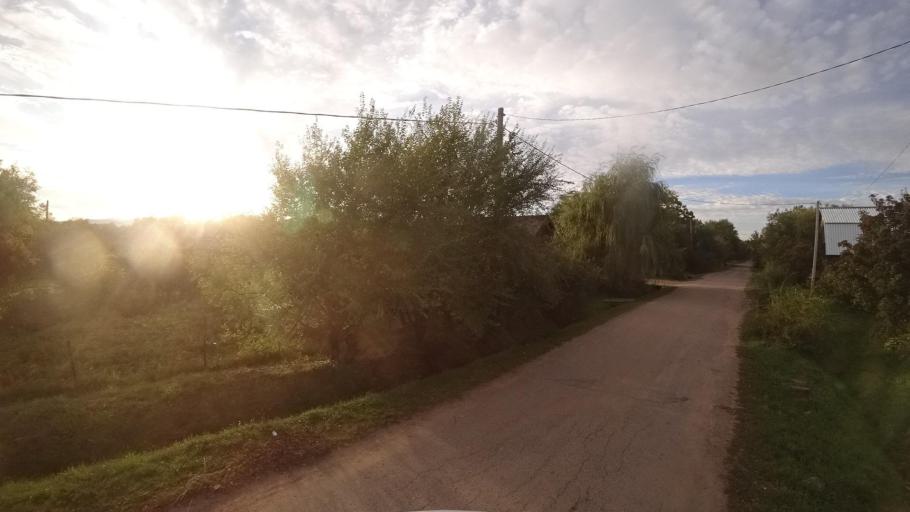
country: RU
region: Primorskiy
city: Yakovlevka
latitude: 44.4306
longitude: 133.4749
